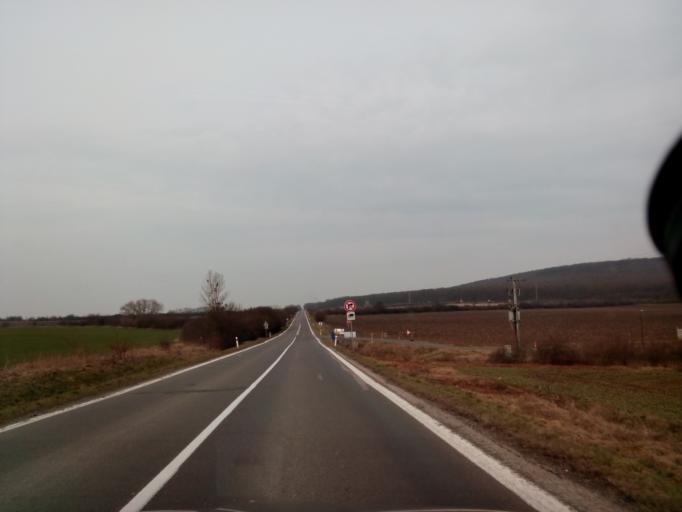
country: HU
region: Borsod-Abauj-Zemplen
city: Satoraljaujhely
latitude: 48.4898
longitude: 21.6479
